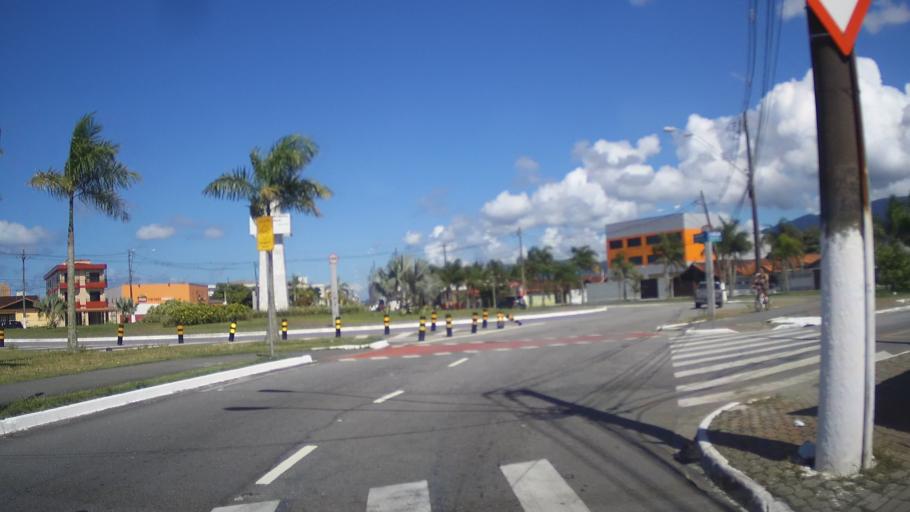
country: BR
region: Sao Paulo
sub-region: Praia Grande
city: Praia Grande
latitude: -24.0363
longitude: -46.5064
